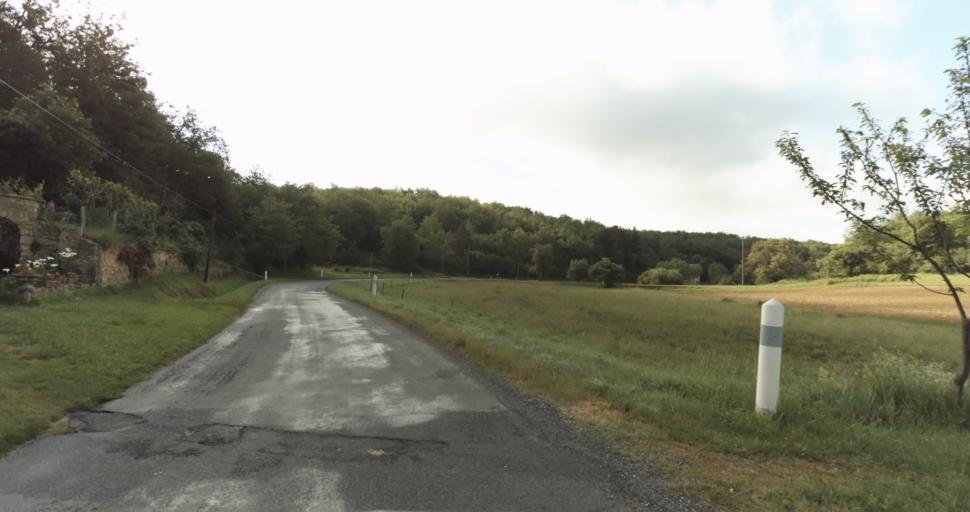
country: FR
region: Aquitaine
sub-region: Departement de la Dordogne
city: Lalinde
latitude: 44.8808
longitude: 0.7774
